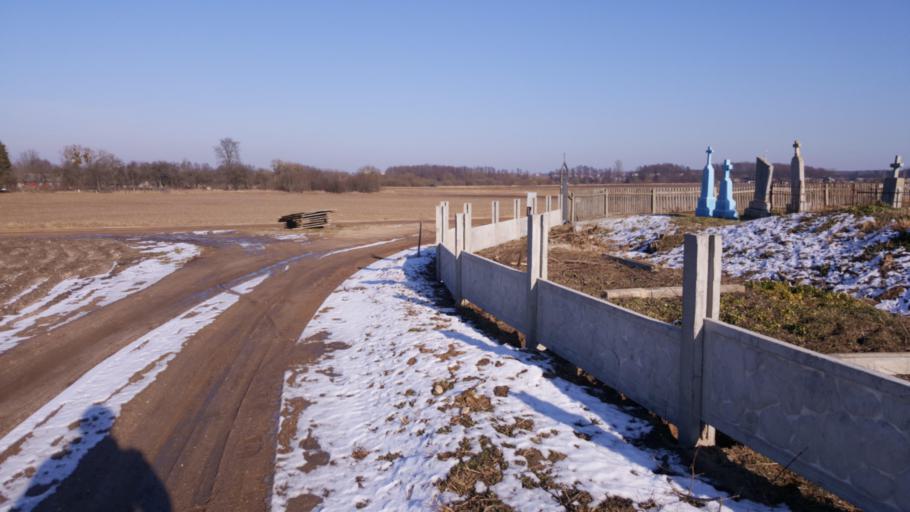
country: BY
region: Brest
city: Kamyanyets
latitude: 52.3827
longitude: 23.7833
